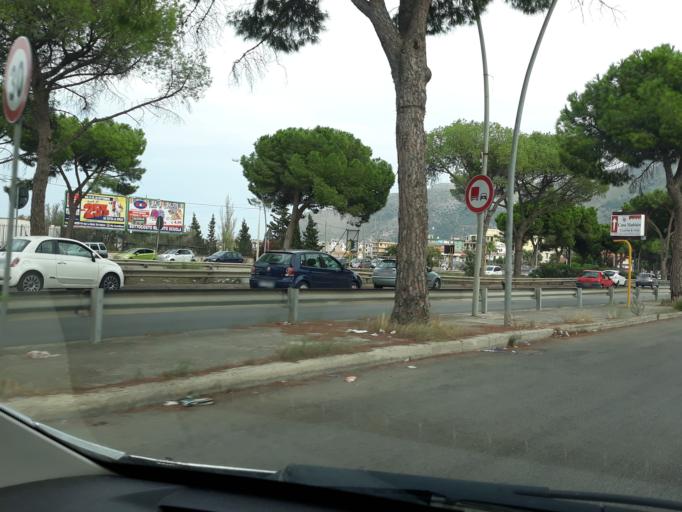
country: IT
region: Sicily
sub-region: Palermo
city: Villa Ciambra
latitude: 38.0889
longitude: 13.3455
